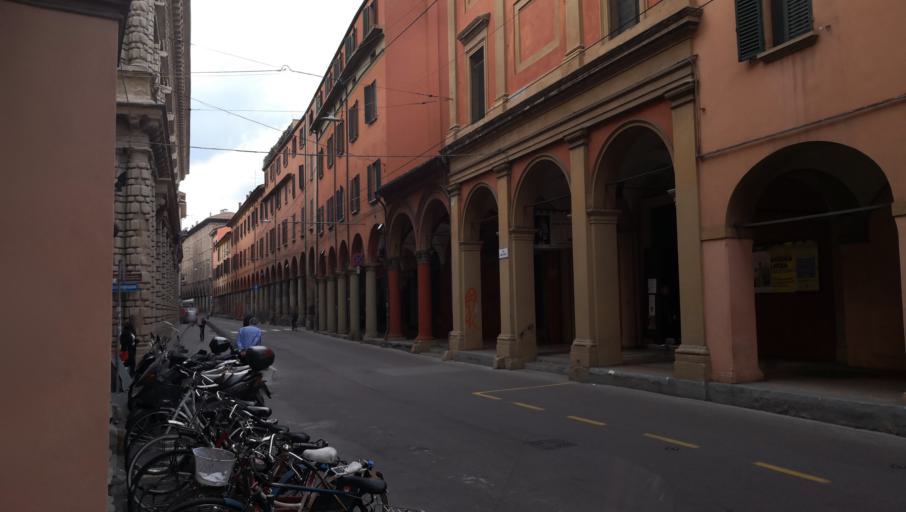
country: IT
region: Emilia-Romagna
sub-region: Provincia di Bologna
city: Bologna
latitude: 44.4943
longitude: 11.3510
